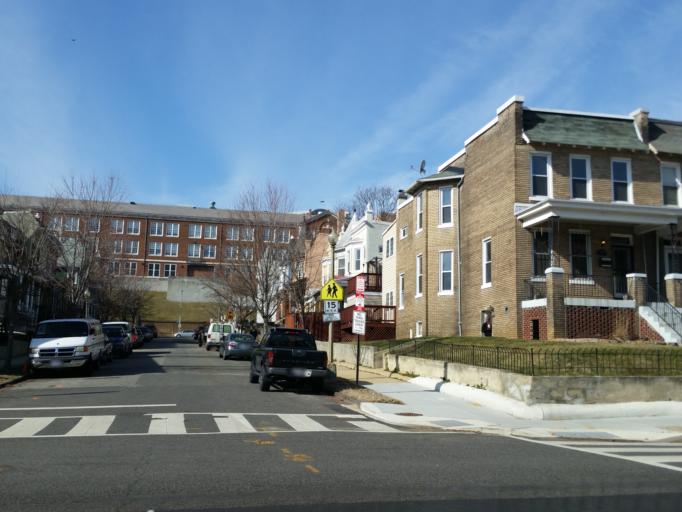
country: US
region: Washington, D.C.
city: Washington, D.C.
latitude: 38.9148
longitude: -77.0020
